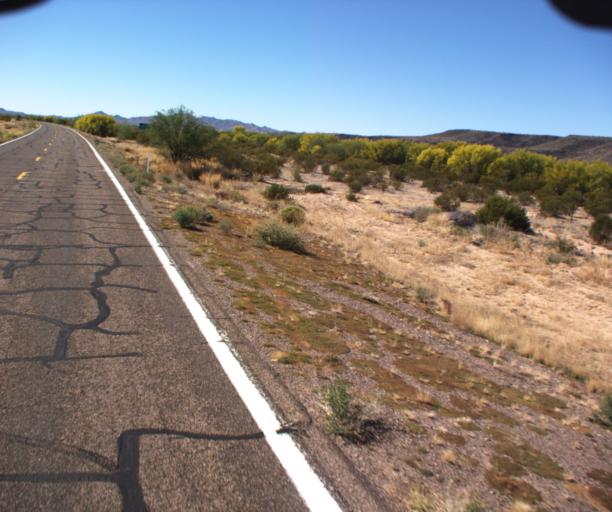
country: US
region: Arizona
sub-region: Pima County
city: Ajo
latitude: 32.4930
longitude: -112.8818
